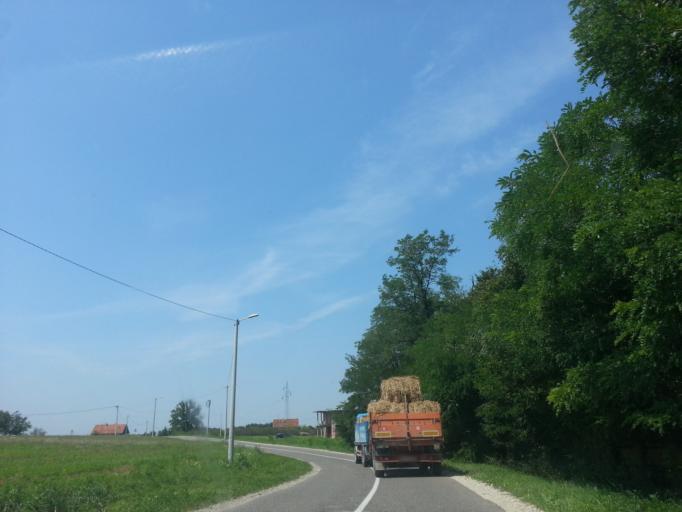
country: BA
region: Brcko
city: Brcko
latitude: 44.8312
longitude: 18.8327
